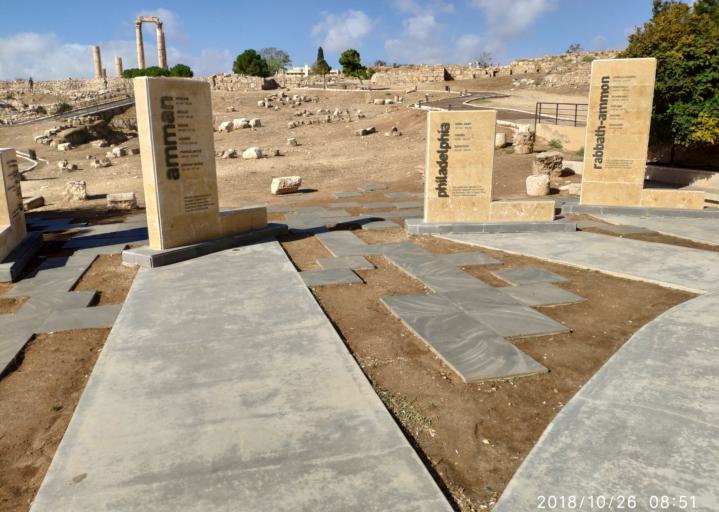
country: JO
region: Amman
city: Amman
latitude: 31.9543
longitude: 35.9366
